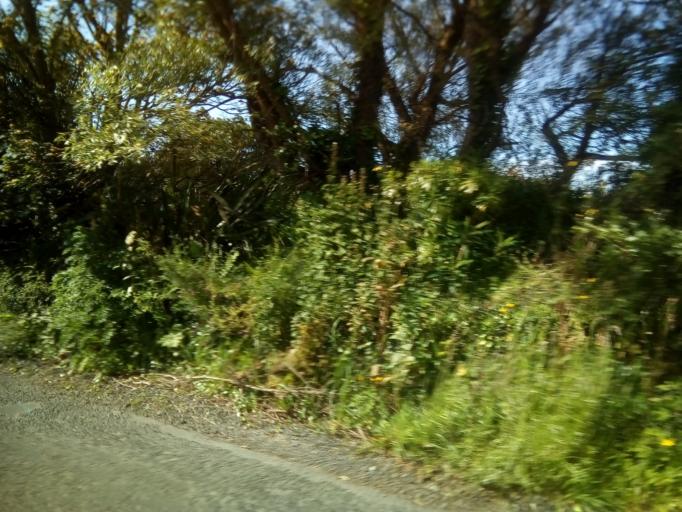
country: IE
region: Leinster
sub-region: Loch Garman
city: Loch Garman
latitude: 52.2248
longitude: -6.5453
